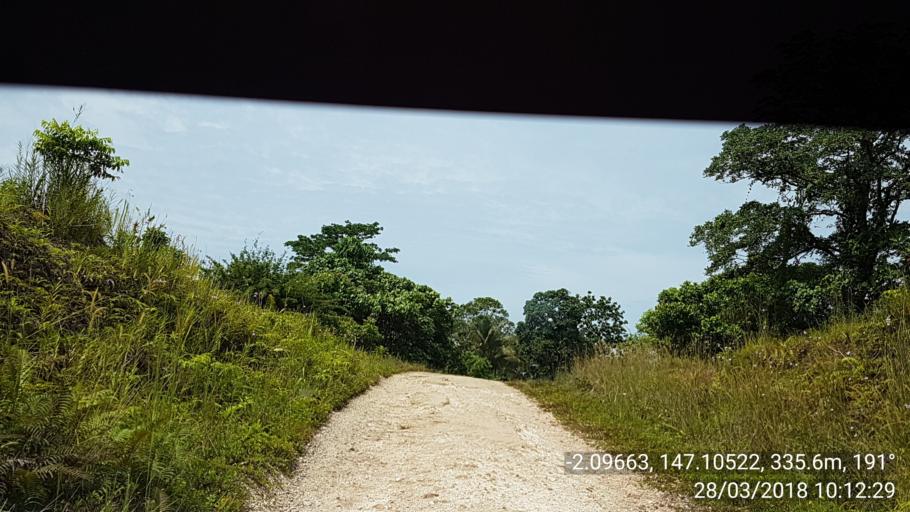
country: PG
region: Manus
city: Lorengau
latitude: -2.0967
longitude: 147.1053
